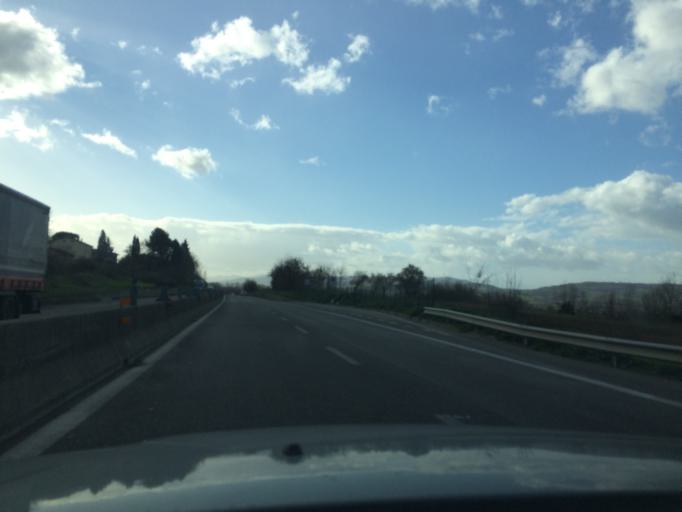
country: IT
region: Umbria
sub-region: Provincia di Perugia
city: Collepepe
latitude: 42.9016
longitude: 12.3898
